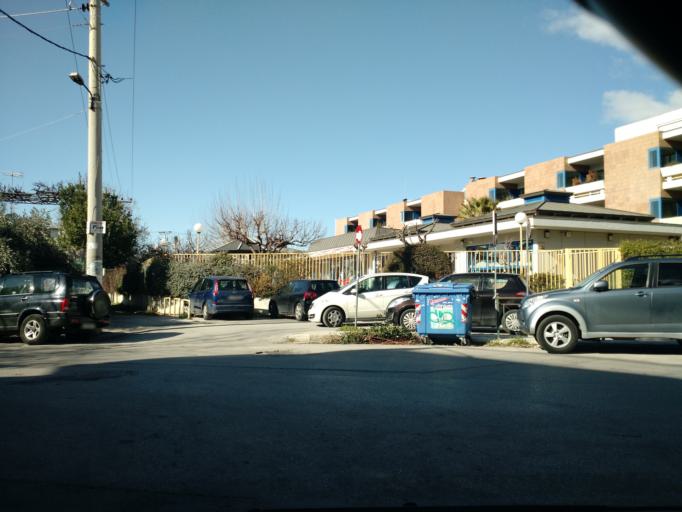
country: GR
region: Attica
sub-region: Nomarchia Athinas
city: Agia Paraskevi
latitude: 38.0205
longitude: 23.8213
